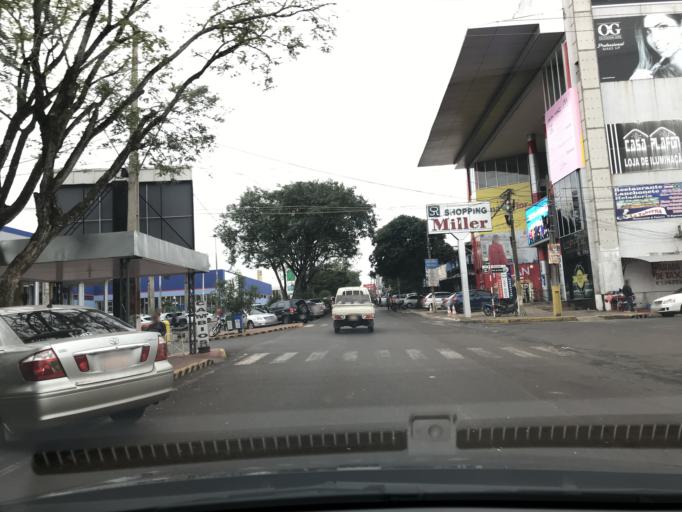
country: PY
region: Canindeyu
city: Salto del Guaira
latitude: -24.0577
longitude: -54.3067
